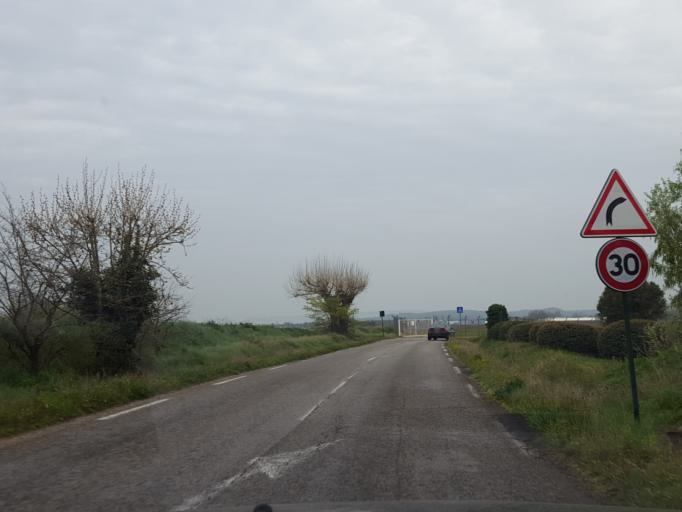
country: FR
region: Provence-Alpes-Cote d'Azur
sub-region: Departement du Vaucluse
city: Morieres-les-Avignon
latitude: 43.9180
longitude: 4.8995
